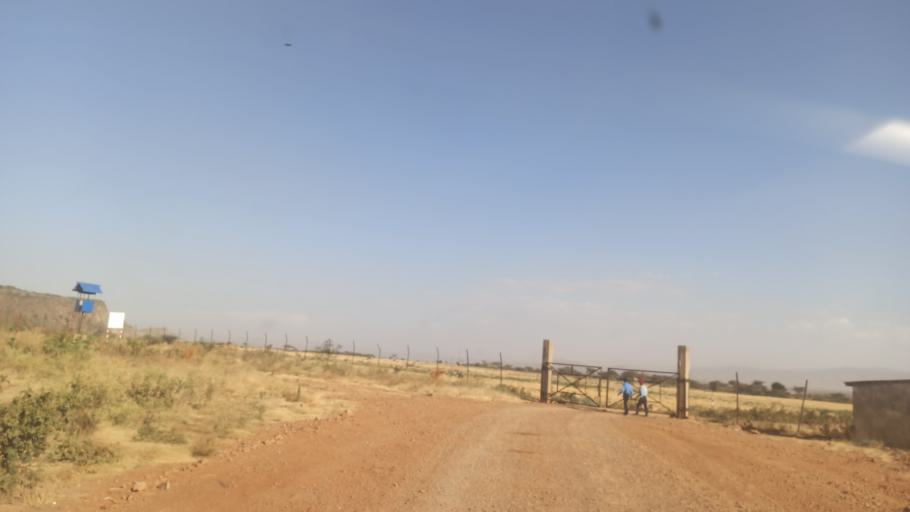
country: ET
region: Oromiya
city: Ziway
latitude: 7.9339
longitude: 38.6215
